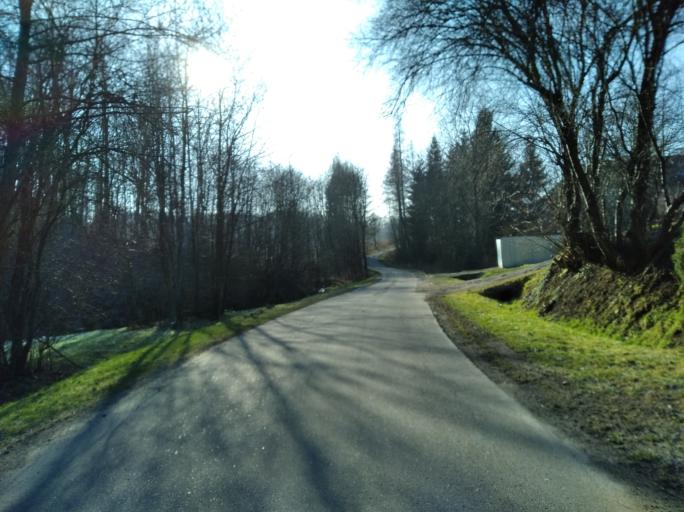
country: PL
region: Subcarpathian Voivodeship
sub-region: Powiat strzyzowski
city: Konieczkowa
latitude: 49.8551
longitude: 21.9286
